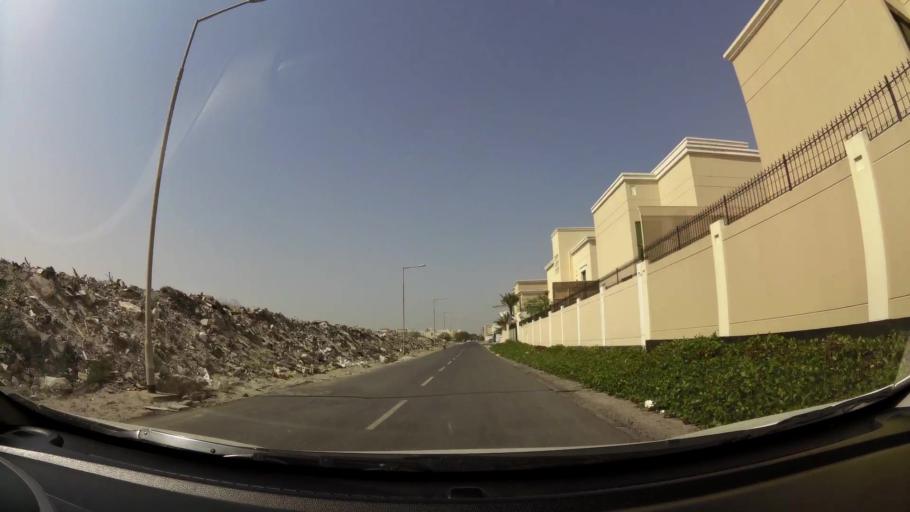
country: BH
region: Manama
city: Jidd Hafs
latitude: 26.2040
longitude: 50.4653
